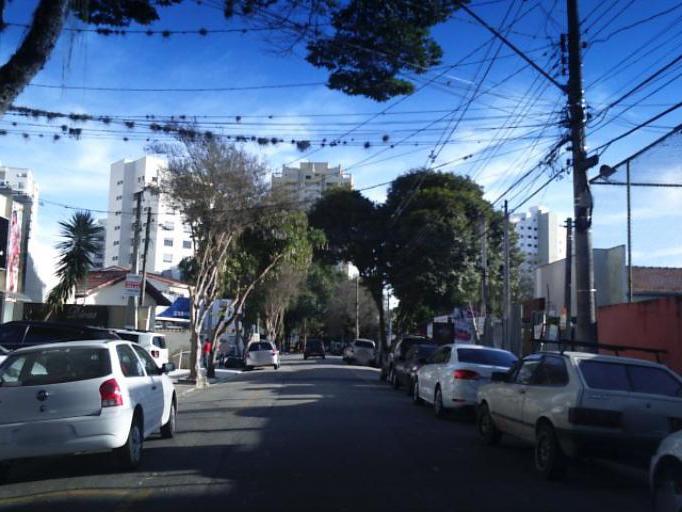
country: BR
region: Sao Paulo
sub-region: Sao Jose Dos Campos
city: Sao Jose dos Campos
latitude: -23.2060
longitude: -45.9011
